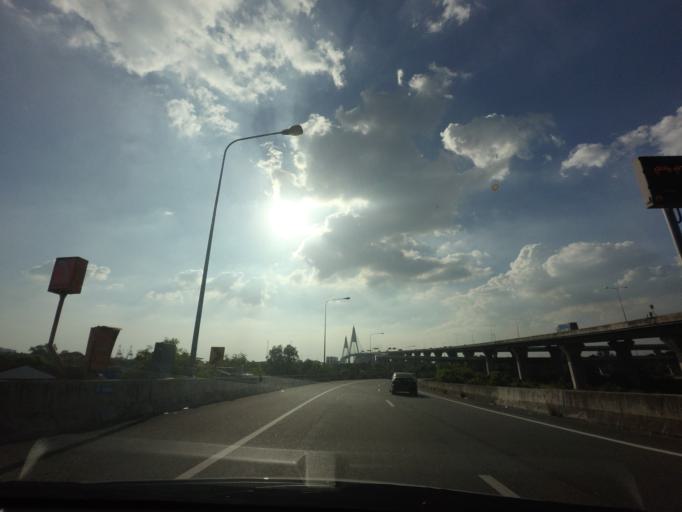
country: TH
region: Samut Prakan
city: Phra Pradaeng
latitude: 13.6381
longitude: 100.5523
